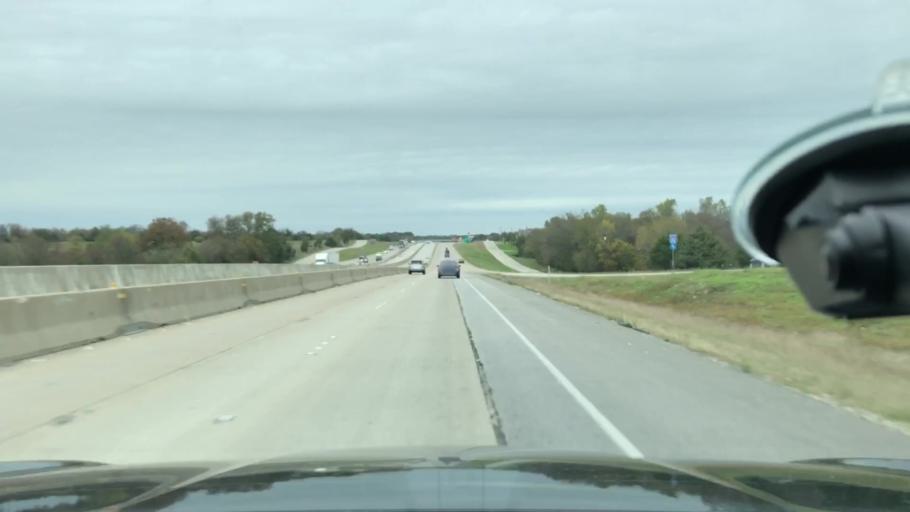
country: US
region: Texas
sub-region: Ellis County
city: Waxahachie
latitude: 32.3856
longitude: -96.8676
